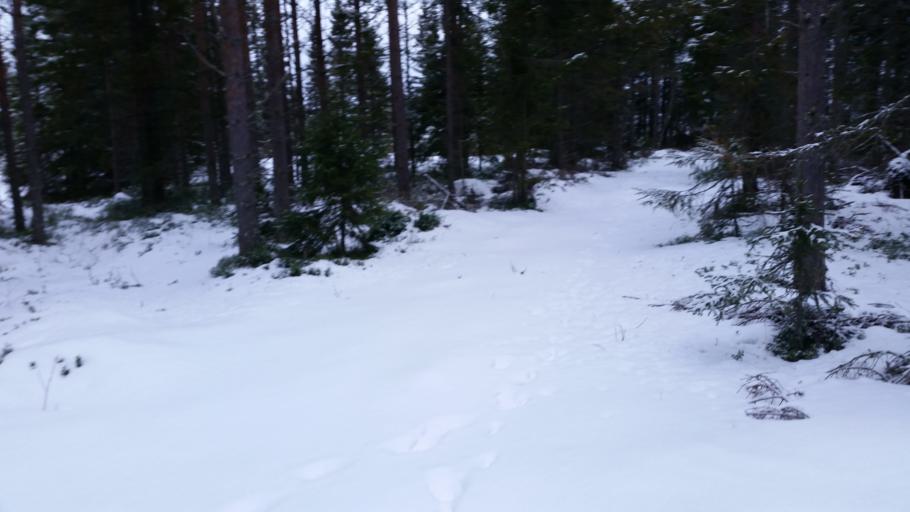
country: SE
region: Vaesterbotten
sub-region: Umea Kommun
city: Saevar
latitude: 63.9156
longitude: 20.7941
